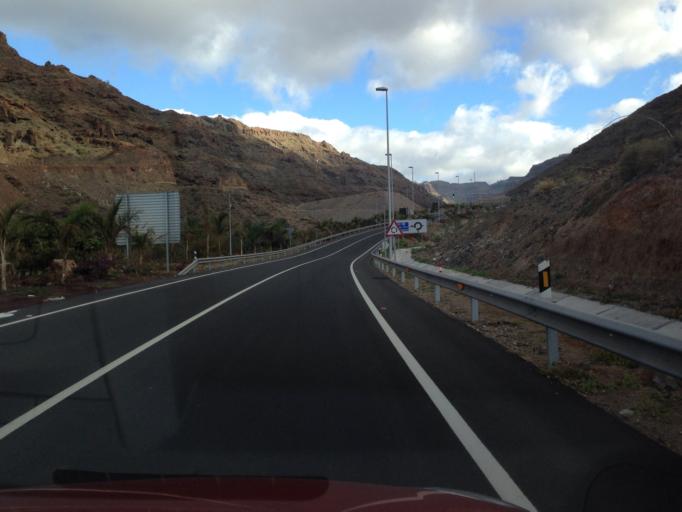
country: ES
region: Canary Islands
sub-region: Provincia de Las Palmas
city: Puerto Rico
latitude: 27.8217
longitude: -15.7492
